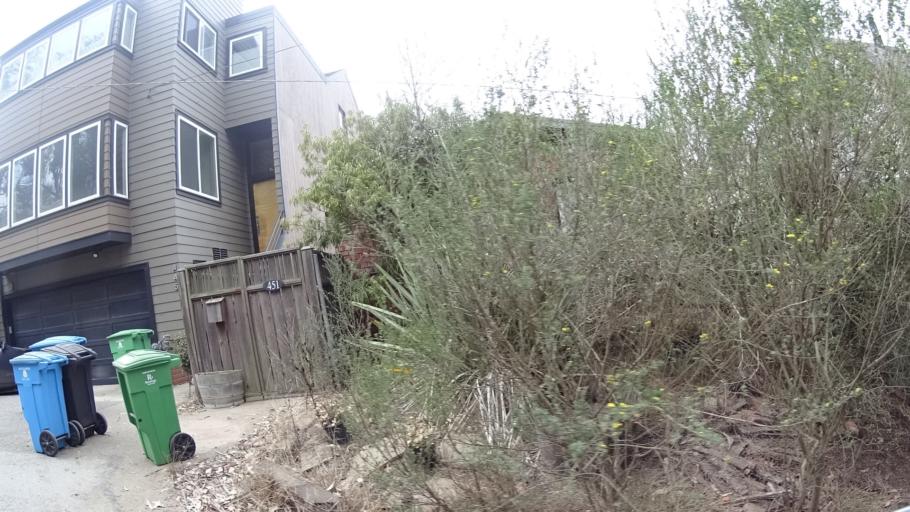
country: US
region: California
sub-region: San Mateo County
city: Daly City
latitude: 37.7339
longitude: -122.4397
